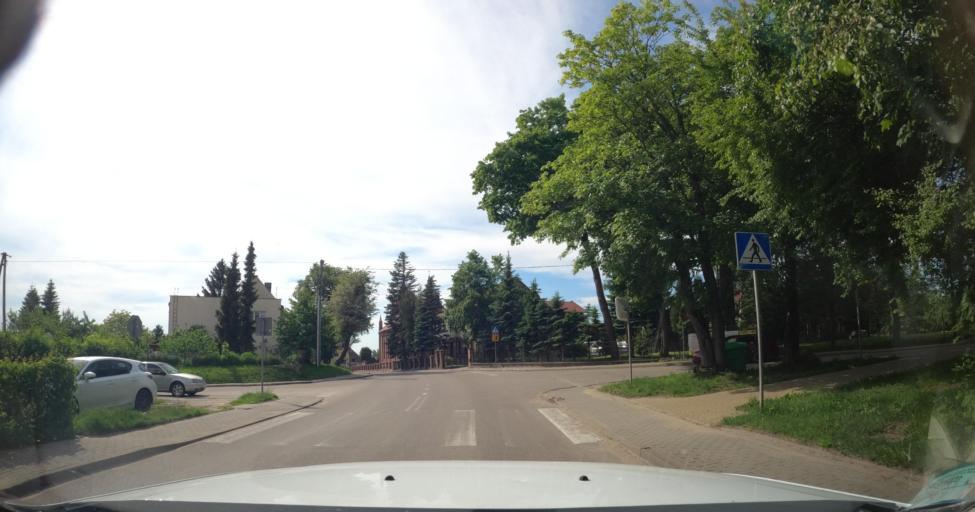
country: PL
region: Warmian-Masurian Voivodeship
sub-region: Powiat ostrodzki
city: Milakowo
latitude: 54.0093
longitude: 20.0767
